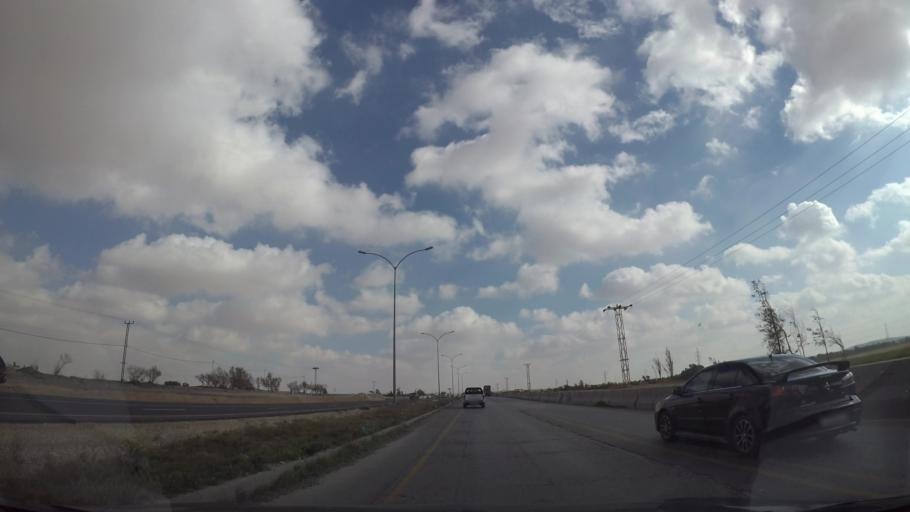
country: JO
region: Amman
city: Al Jizah
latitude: 31.6755
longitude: 35.9677
